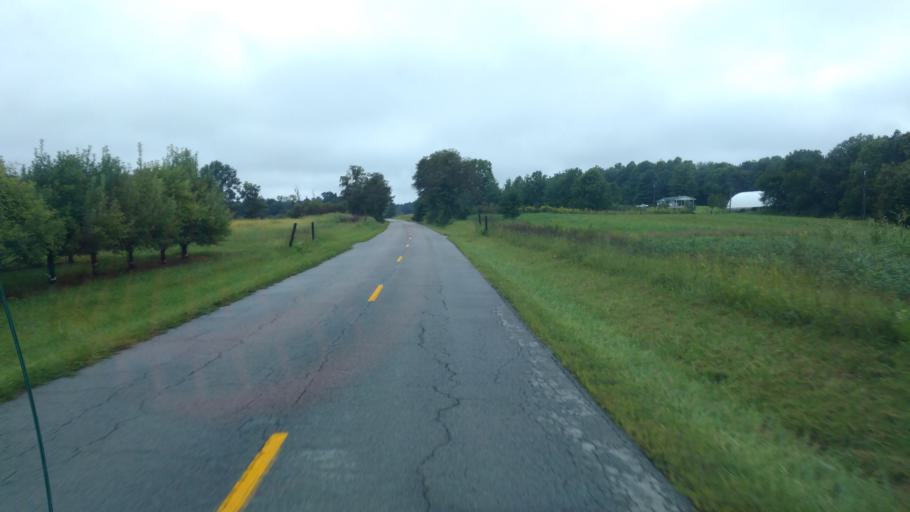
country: US
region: Kentucky
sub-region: Fleming County
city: Flemingsburg
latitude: 38.4171
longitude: -83.5521
